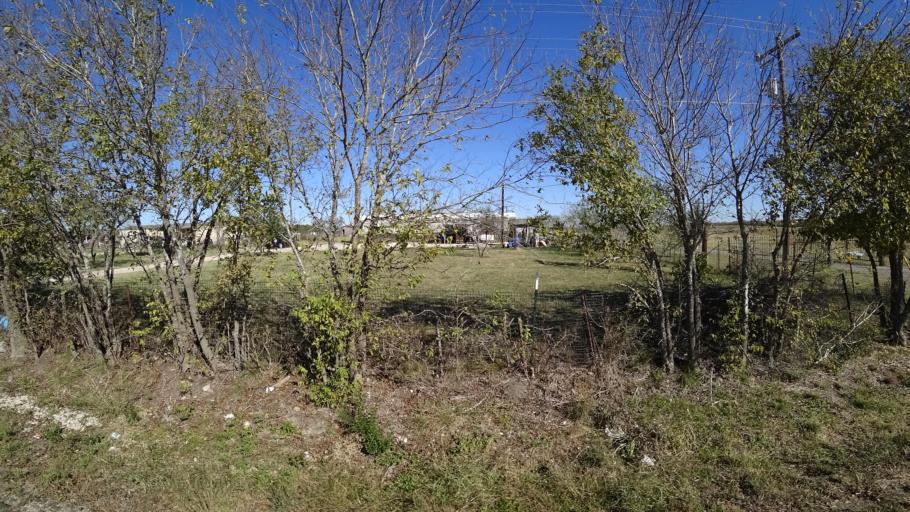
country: US
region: Texas
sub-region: Travis County
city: Garfield
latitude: 30.1176
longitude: -97.5915
